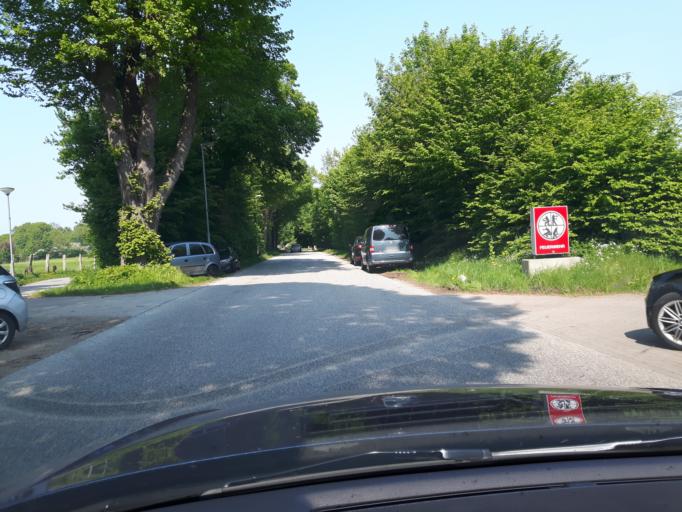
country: DE
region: Schleswig-Holstein
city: Travemuende
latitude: 53.9351
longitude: 10.8387
